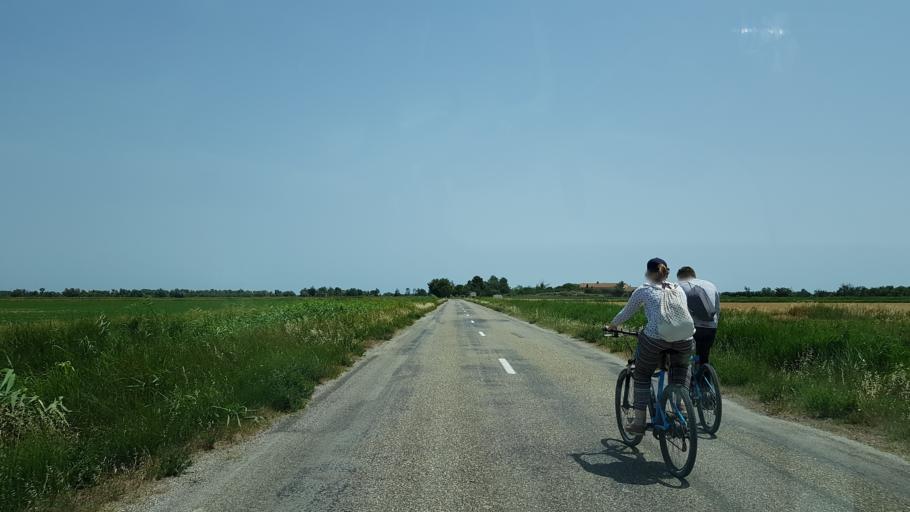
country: FR
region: Provence-Alpes-Cote d'Azur
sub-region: Departement des Bouches-du-Rhone
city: Port-Saint-Louis-du-Rhone
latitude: 43.4340
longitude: 4.6865
